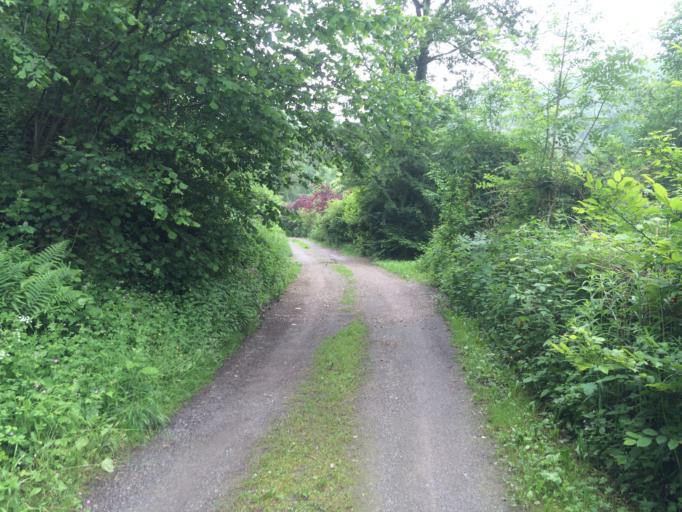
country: BE
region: Wallonia
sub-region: Province de Namur
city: Yvoir
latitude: 50.3220
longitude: 4.9445
